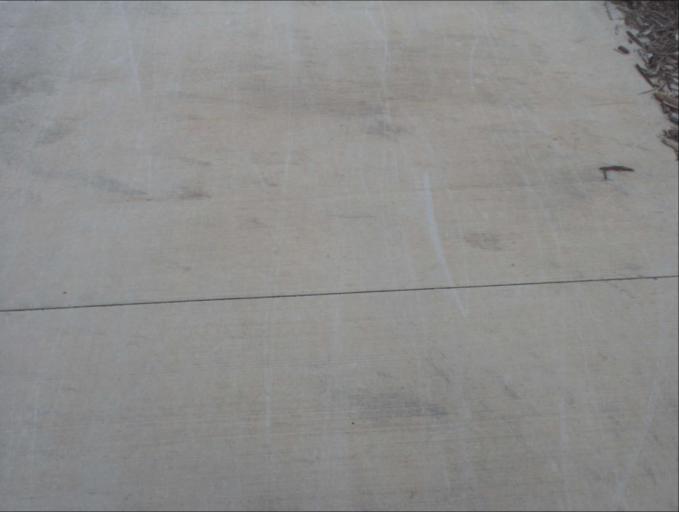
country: AU
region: Queensland
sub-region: Logan
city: Chambers Flat
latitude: -27.8084
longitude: 153.1104
